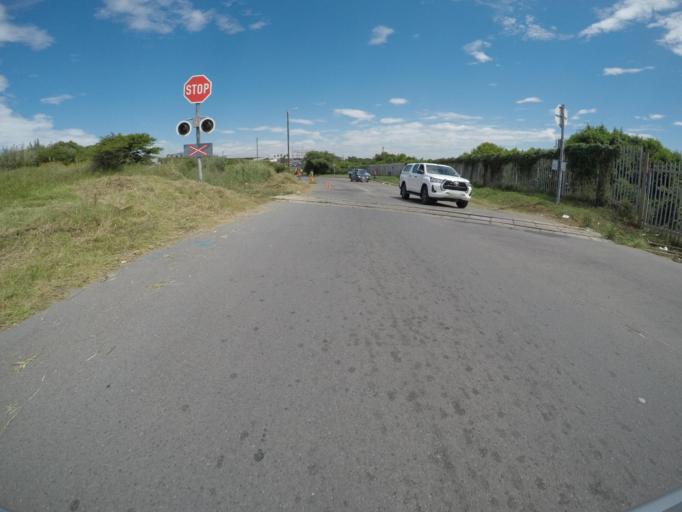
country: ZA
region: Eastern Cape
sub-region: Buffalo City Metropolitan Municipality
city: East London
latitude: -33.0285
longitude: 27.9043
